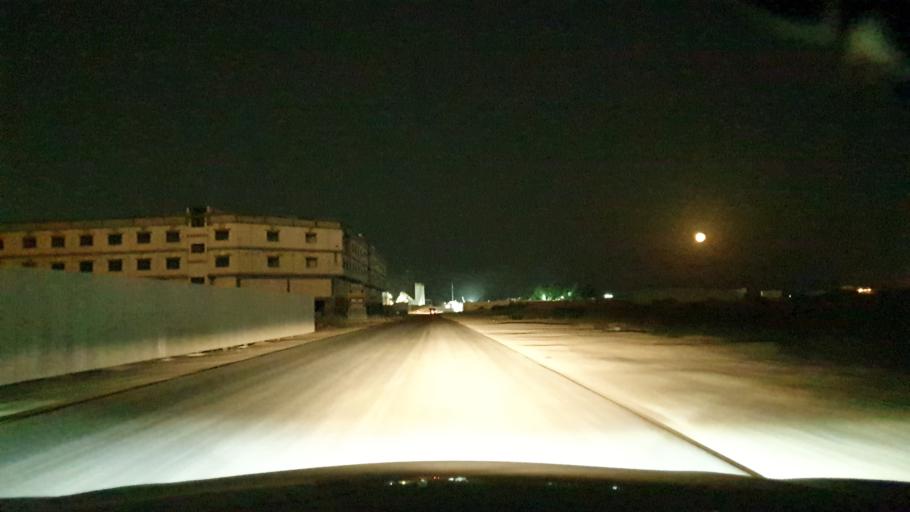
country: BH
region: Northern
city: Sitrah
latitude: 26.0871
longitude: 50.6142
